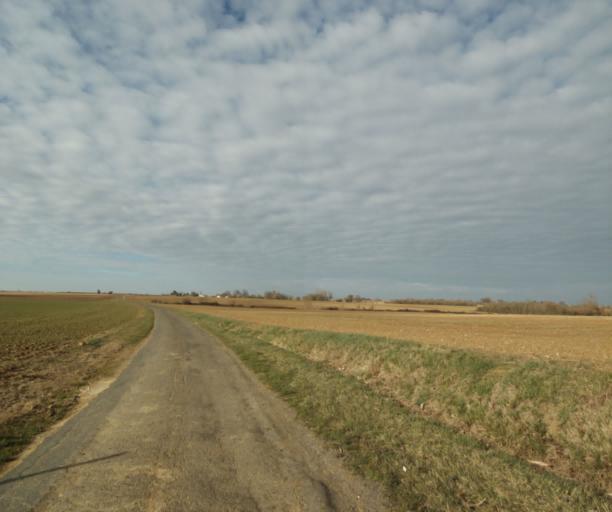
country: FR
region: Poitou-Charentes
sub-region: Departement de la Charente-Maritime
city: Corme-Royal
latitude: 45.7296
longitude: -0.7946
